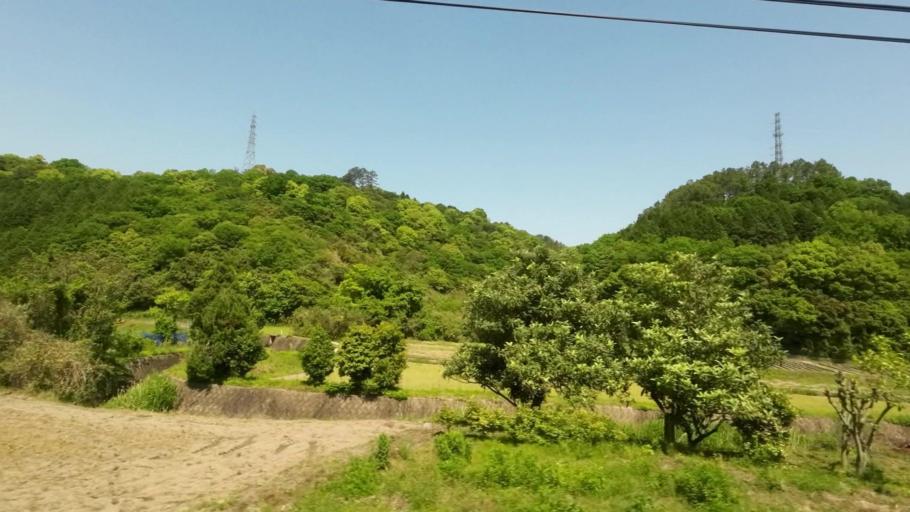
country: JP
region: Ehime
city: Niihama
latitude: 33.9351
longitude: 133.2744
